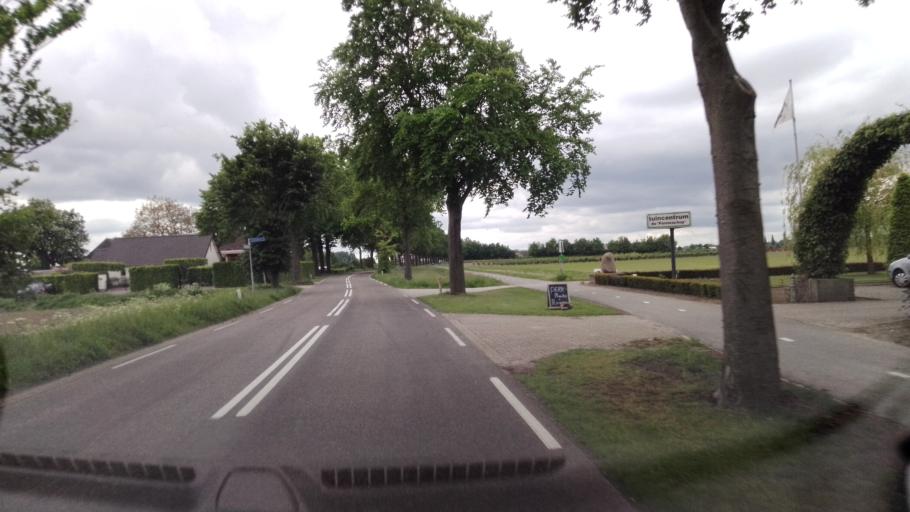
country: NL
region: Limburg
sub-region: Gemeente Venlo
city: Arcen
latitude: 51.4350
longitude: 6.1485
